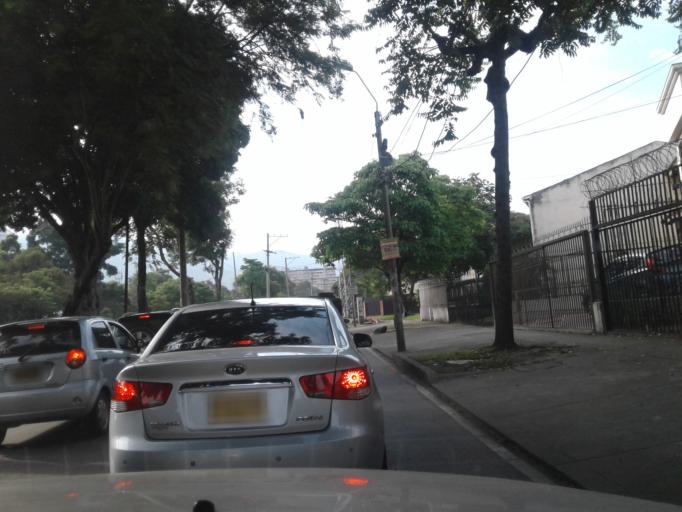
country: CO
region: Valle del Cauca
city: Cali
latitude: 3.4697
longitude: -76.5233
